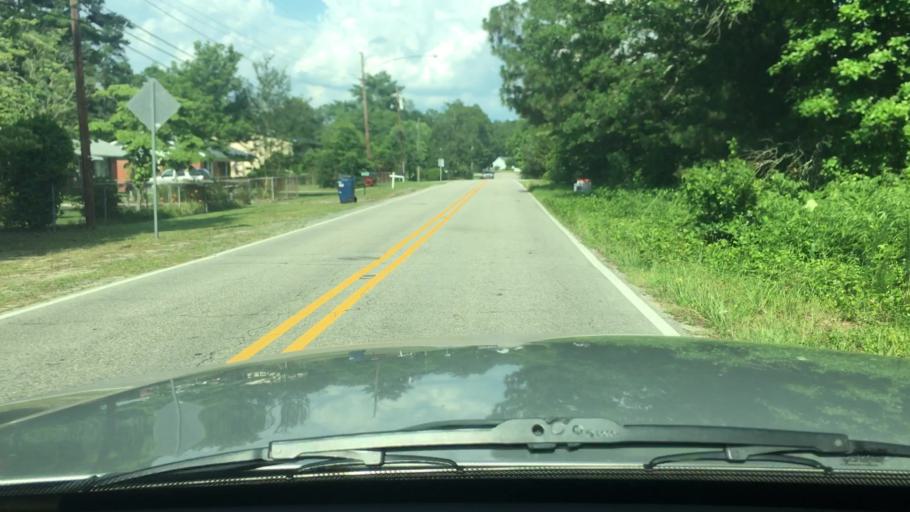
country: US
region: North Carolina
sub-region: Cumberland County
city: Fayetteville
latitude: 35.1112
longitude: -78.8718
